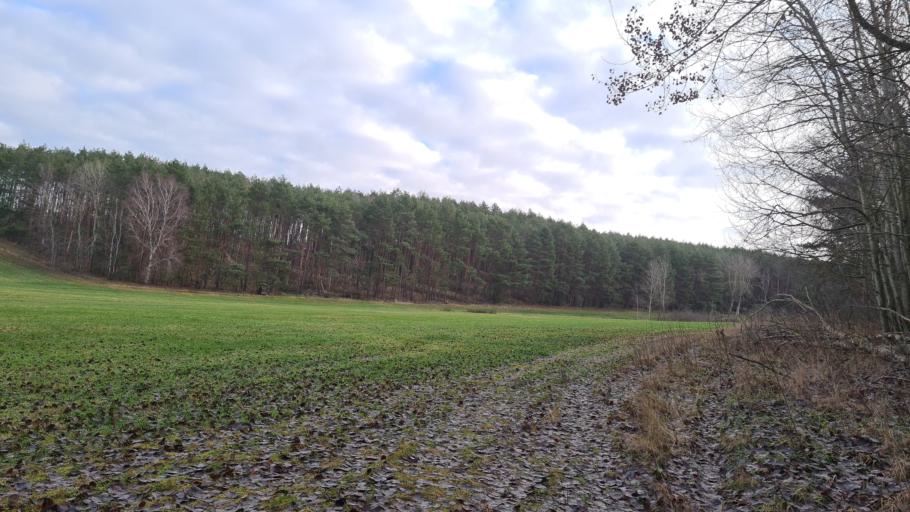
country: DE
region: Brandenburg
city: Groden
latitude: 51.3939
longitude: 13.5762
